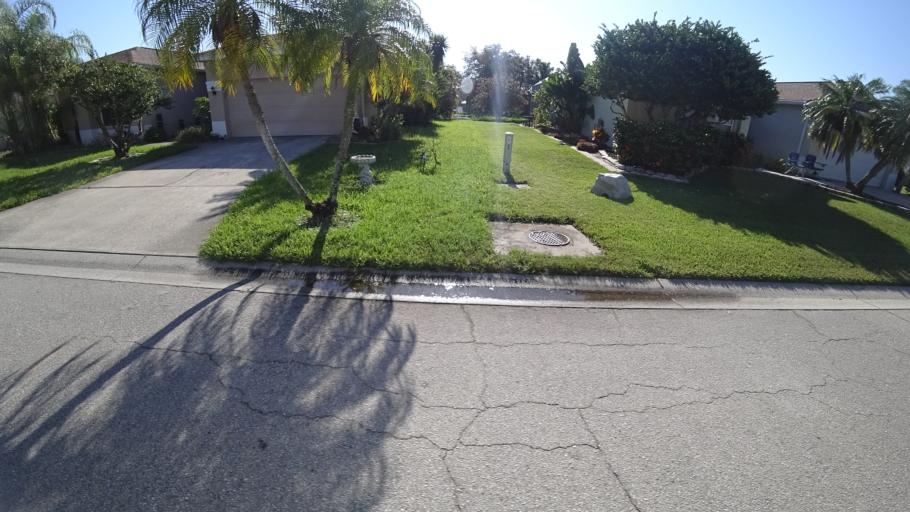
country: US
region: Florida
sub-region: Manatee County
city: Ellenton
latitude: 27.5034
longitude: -82.5129
